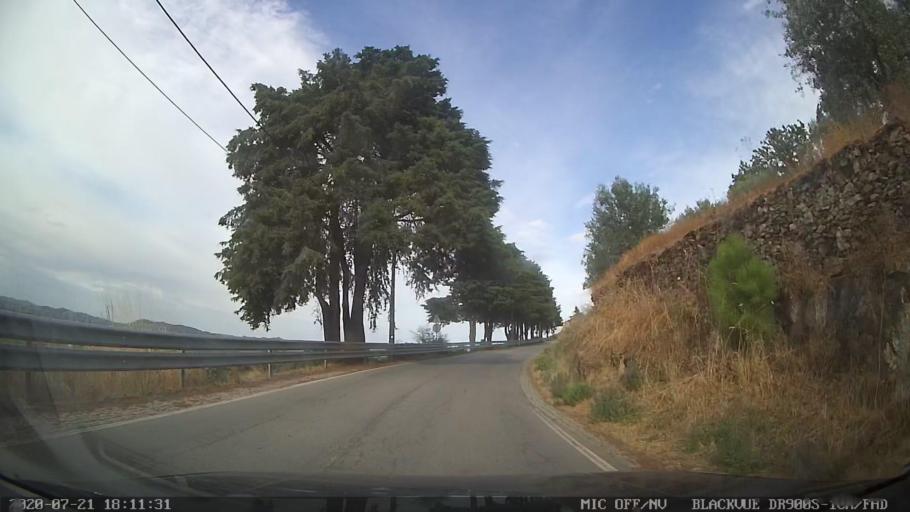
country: PT
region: Viseu
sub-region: Sao Joao da Pesqueira
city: Sao Joao da Pesqueira
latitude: 41.1417
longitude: -7.3991
